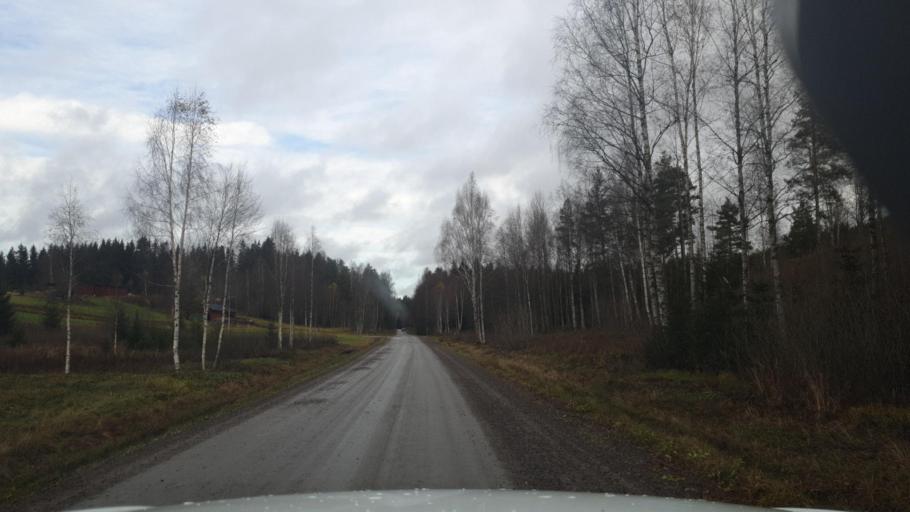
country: NO
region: Hedmark
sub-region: Eidskog
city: Skotterud
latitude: 59.8491
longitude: 11.9847
